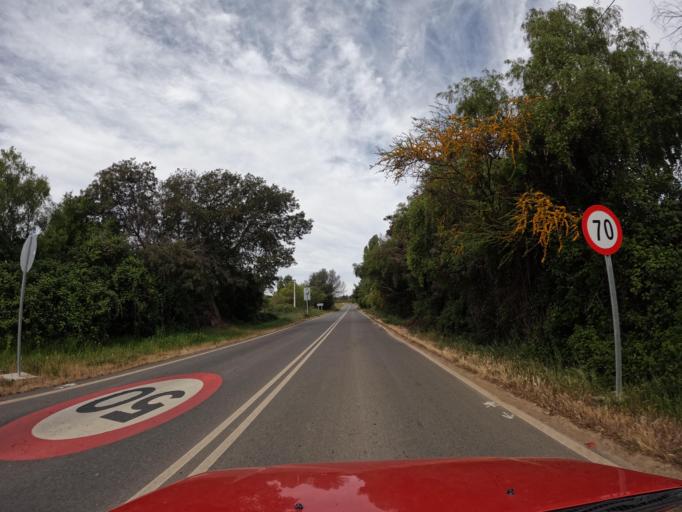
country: CL
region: Maule
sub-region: Provincia de Talca
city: Talca
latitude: -35.3227
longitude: -71.9526
